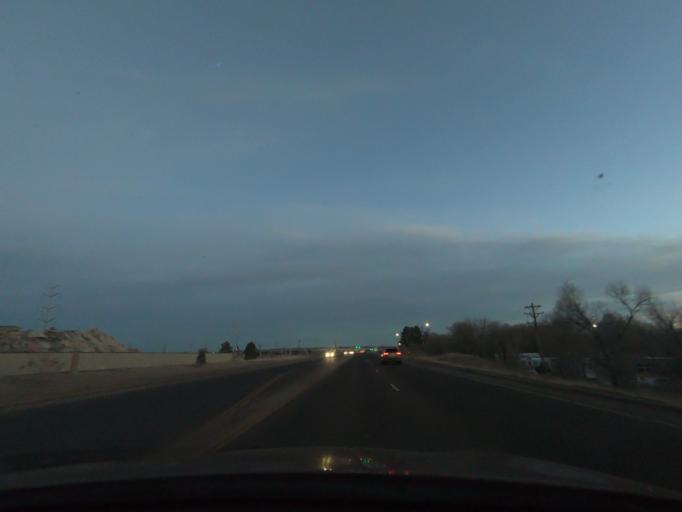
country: US
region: Colorado
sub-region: El Paso County
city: Stratmoor
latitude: 38.7715
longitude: -104.7646
